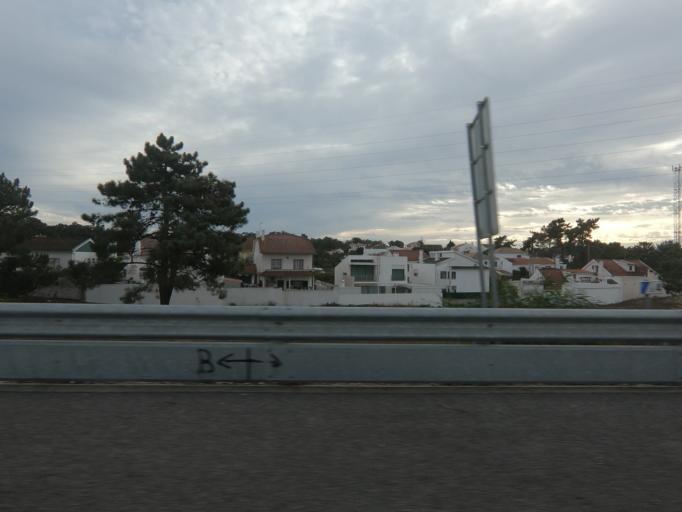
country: PT
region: Setubal
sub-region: Almada
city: Charneca
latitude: 38.6169
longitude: -9.1769
